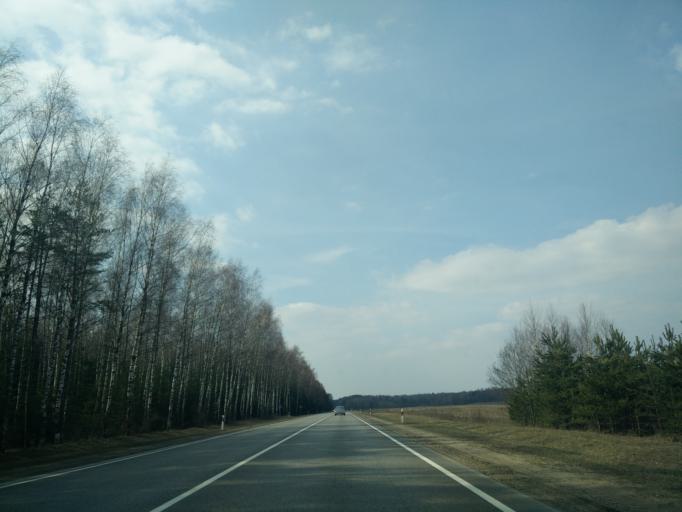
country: LT
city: Lentvaris
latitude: 54.6220
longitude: 25.0420
